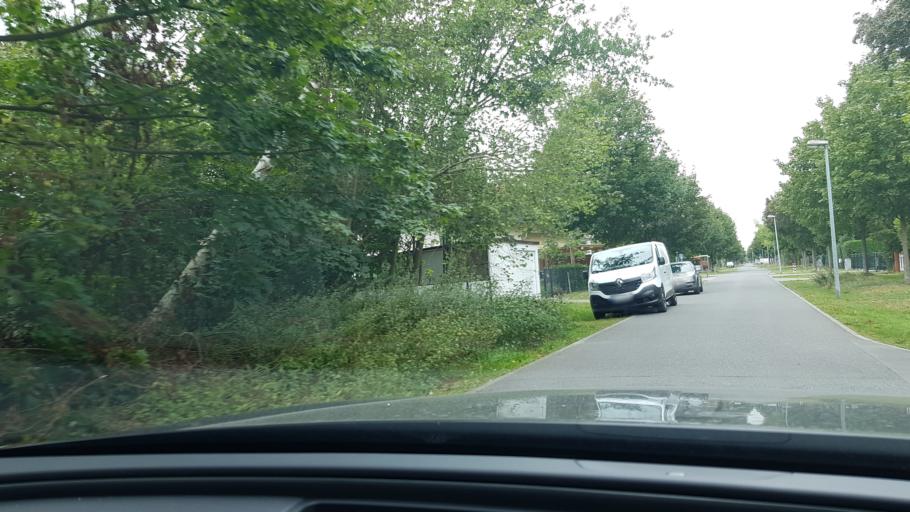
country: DE
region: Brandenburg
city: Brieselang
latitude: 52.5957
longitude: 13.0026
